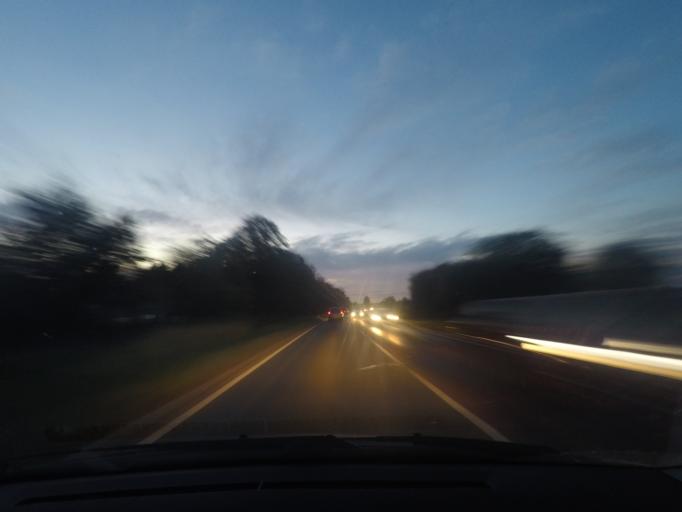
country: GB
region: England
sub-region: East Riding of Yorkshire
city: Wilberfoss
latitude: 53.9487
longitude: -0.9008
